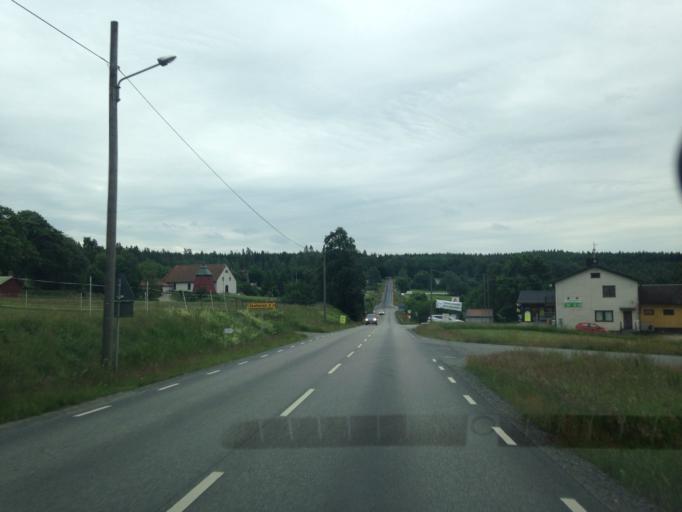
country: SE
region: Vaestra Goetaland
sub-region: Marks Kommun
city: Bua
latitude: 57.5057
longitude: 12.5484
